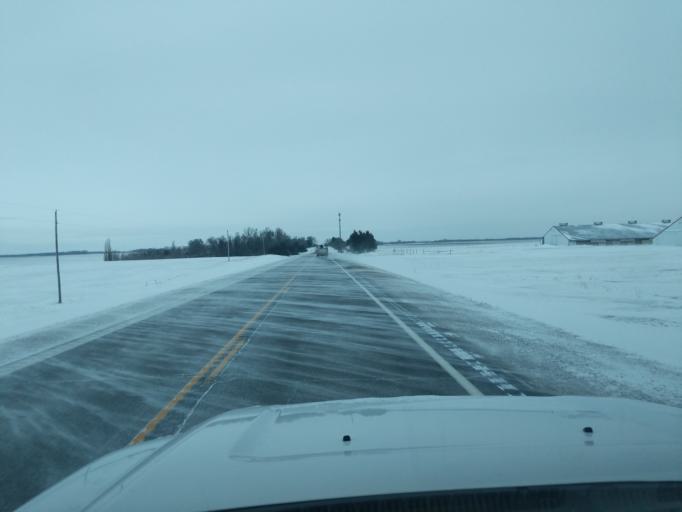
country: US
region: Minnesota
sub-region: Redwood County
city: Redwood Falls
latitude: 44.6063
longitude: -94.9945
